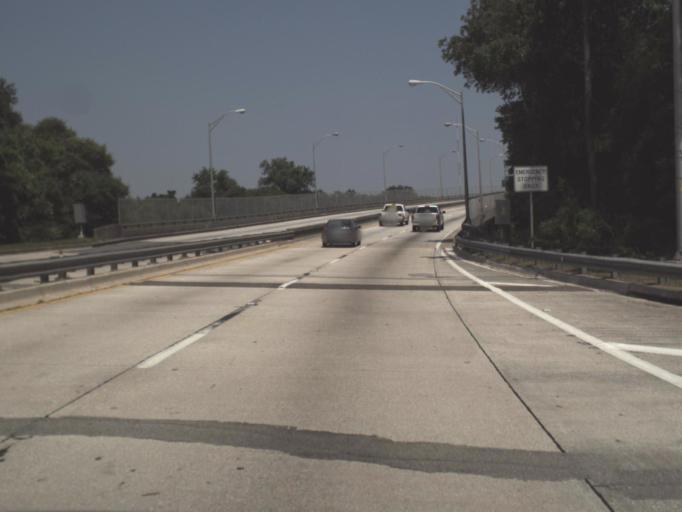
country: US
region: Florida
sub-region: Duval County
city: Jacksonville
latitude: 30.3096
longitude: -81.6224
